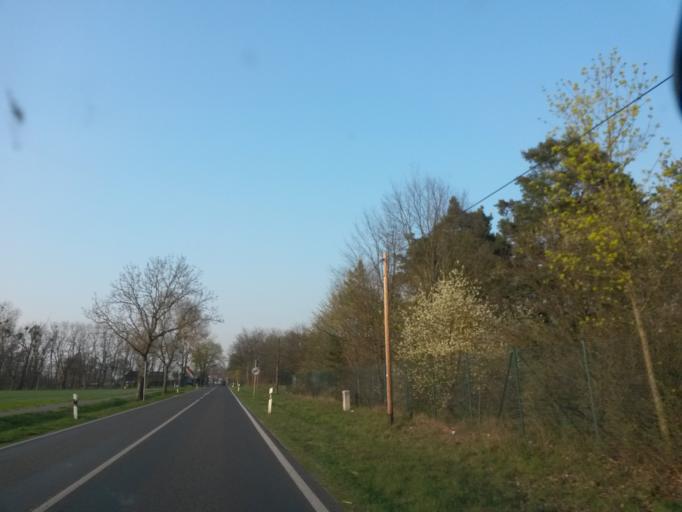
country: DE
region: Brandenburg
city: Rehfelde
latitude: 52.4947
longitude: 13.9190
